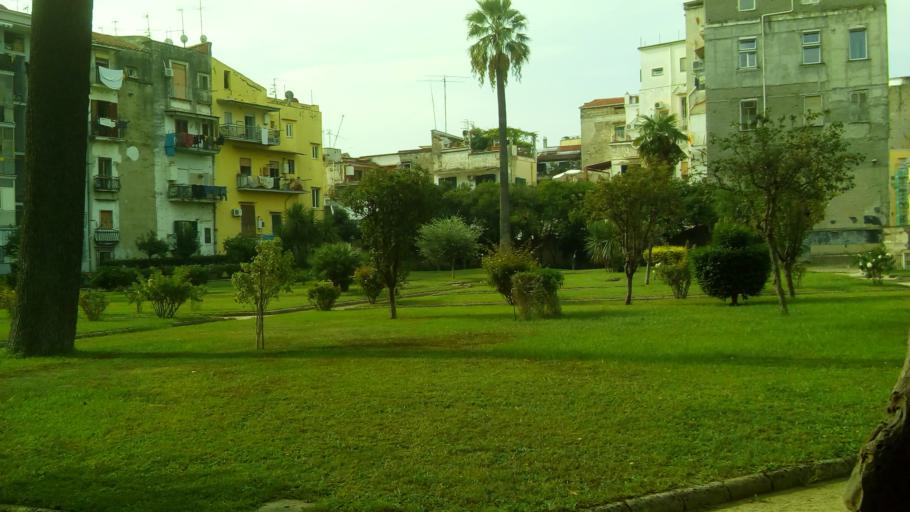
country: IT
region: Campania
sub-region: Provincia di Napoli
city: Napoli
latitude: 40.8566
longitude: 14.2611
